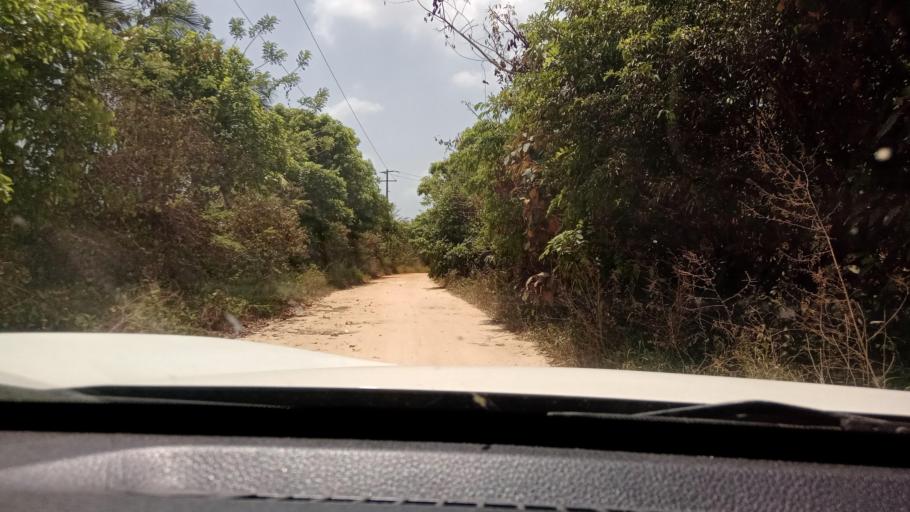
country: MX
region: Veracruz
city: Las Choapas
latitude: 17.9393
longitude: -94.1193
